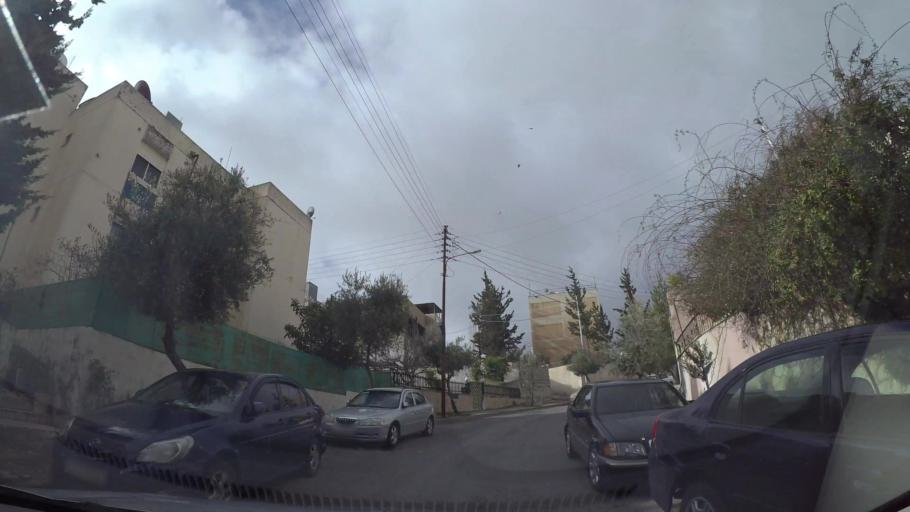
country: JO
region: Amman
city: Al Jubayhah
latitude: 32.0528
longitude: 35.8845
